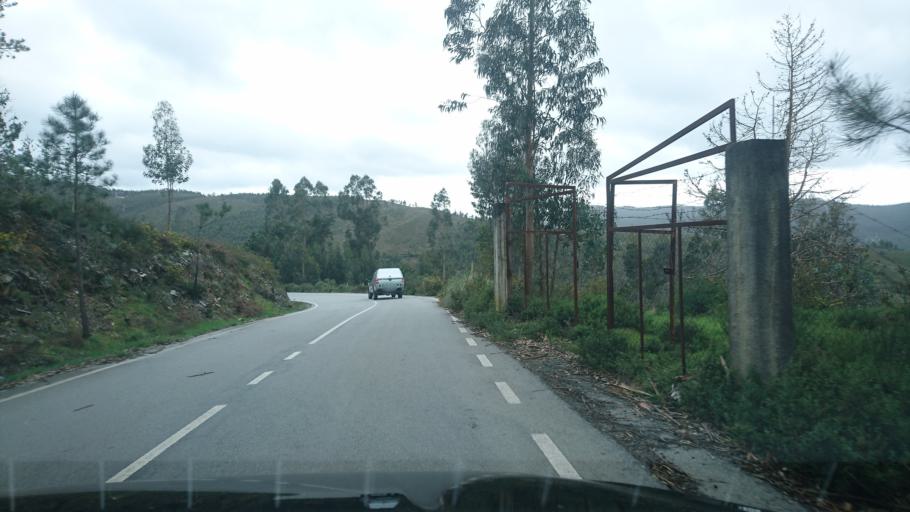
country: PT
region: Porto
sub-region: Paredes
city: Recarei
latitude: 41.1348
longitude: -8.4020
